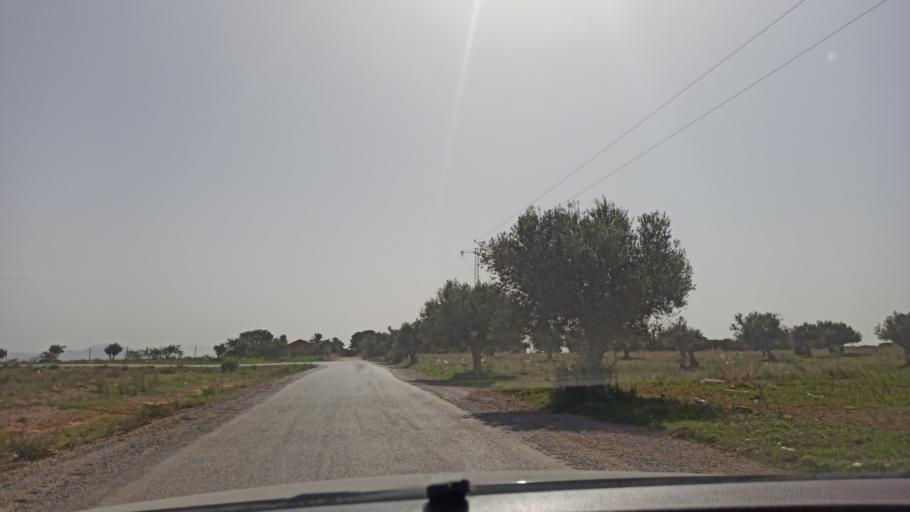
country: TN
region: Manouba
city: Manouba
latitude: 36.7339
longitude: 10.0869
